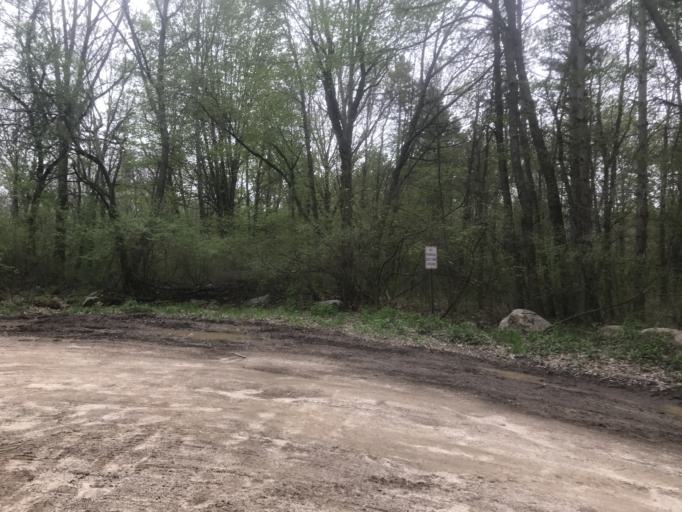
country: US
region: Michigan
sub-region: Ionia County
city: Portland
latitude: 42.8056
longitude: -84.9097
